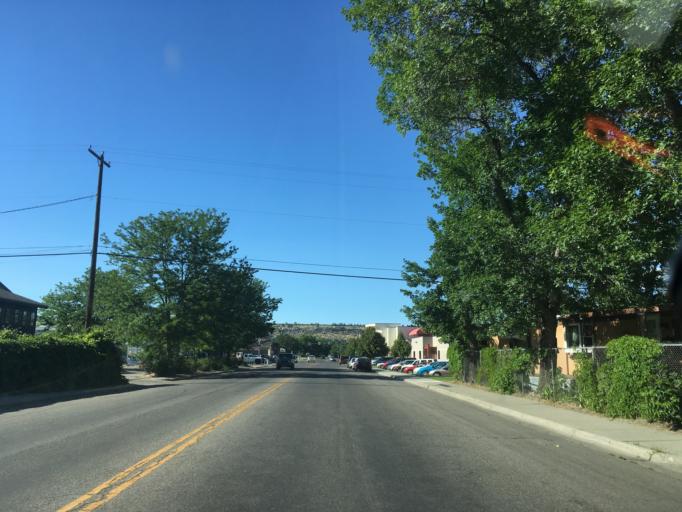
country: US
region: Montana
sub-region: Yellowstone County
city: Billings
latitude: 45.7819
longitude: -108.5538
